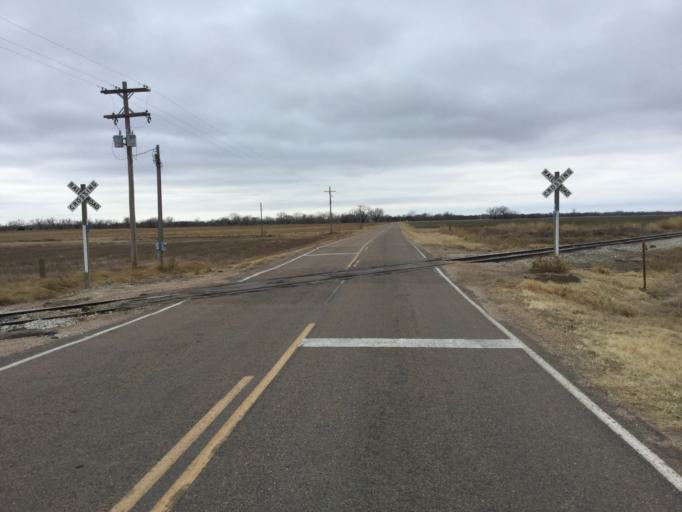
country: US
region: Kansas
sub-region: Barton County
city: Ellinwood
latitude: 38.2893
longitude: -98.4415
